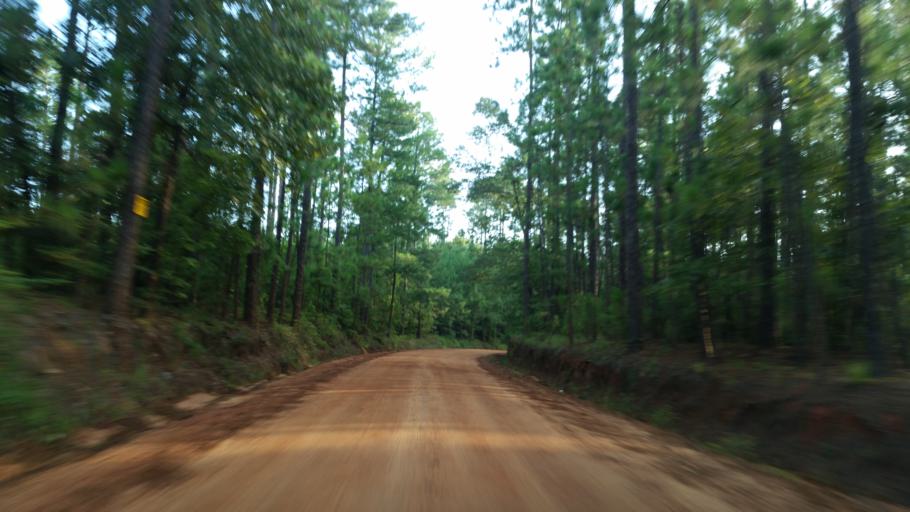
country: US
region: Alabama
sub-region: Escambia County
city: Atmore
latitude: 30.9598
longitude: -87.5728
